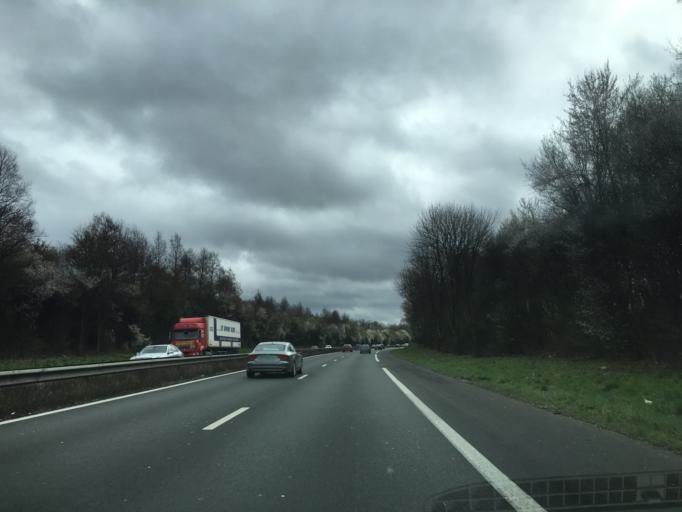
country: FR
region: Ile-de-France
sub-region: Departement de Seine-et-Marne
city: Brie-Comte-Robert
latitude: 48.6815
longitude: 2.6039
